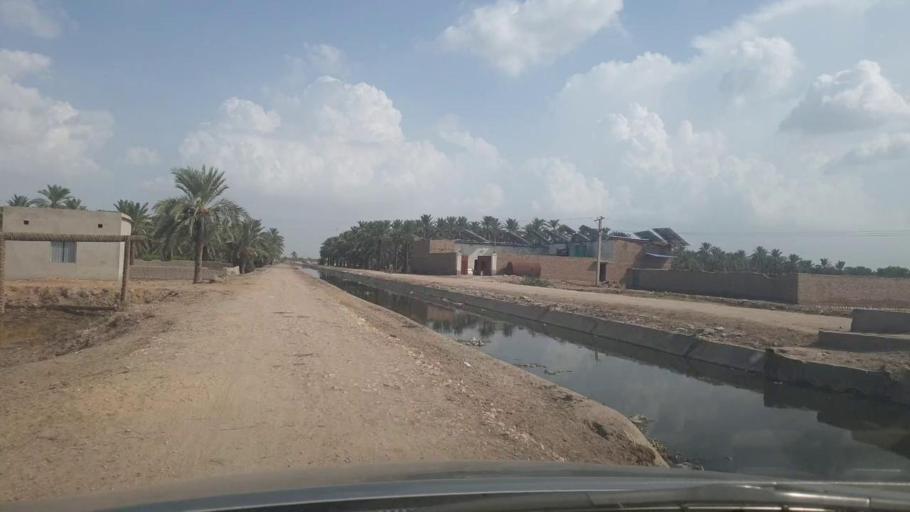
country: PK
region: Sindh
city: Khairpur
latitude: 27.5357
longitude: 68.7750
